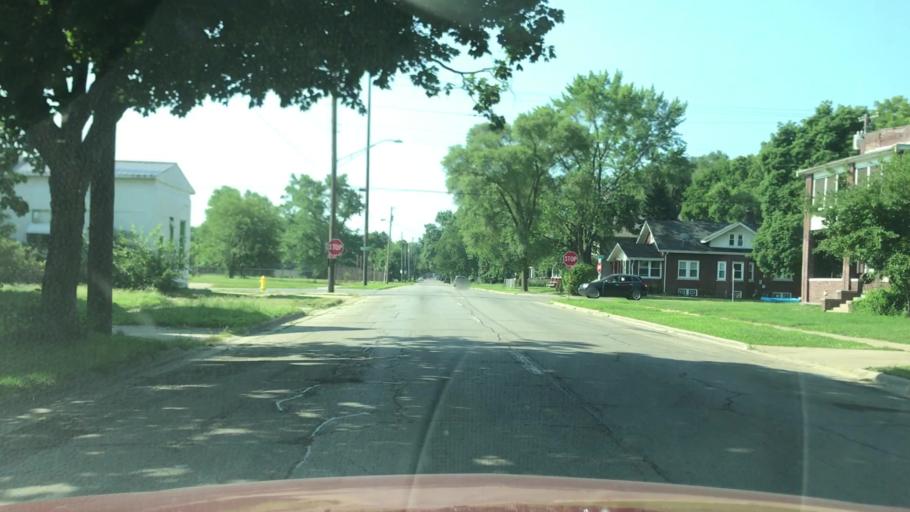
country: US
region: Illinois
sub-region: Winnebago County
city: Rockford
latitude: 42.2485
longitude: -89.0824
